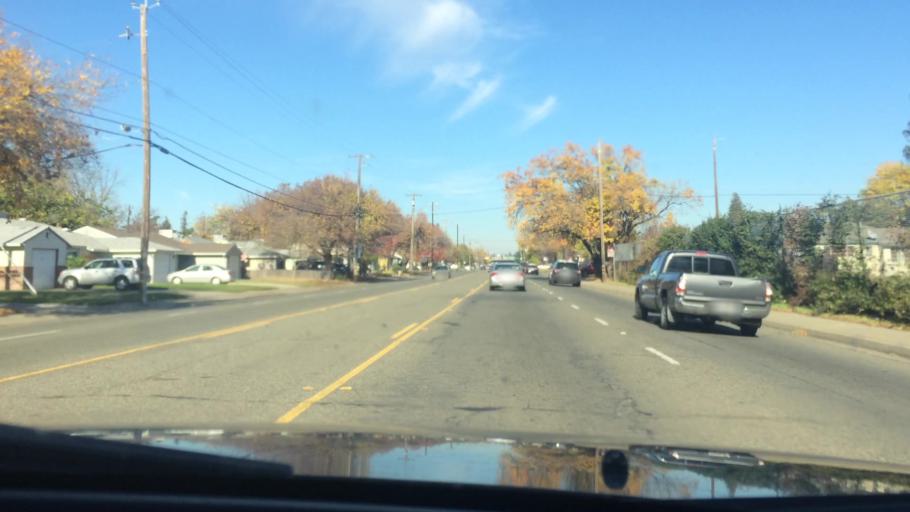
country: US
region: California
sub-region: Sacramento County
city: Florin
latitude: 38.5427
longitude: -121.4278
